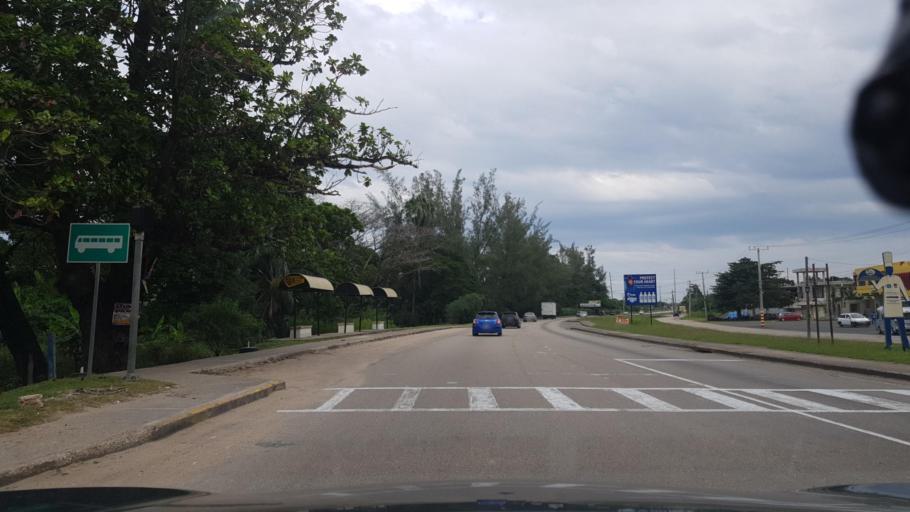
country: JM
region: Saint Ann
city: Runaway Bay
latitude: 18.4641
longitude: -77.3223
